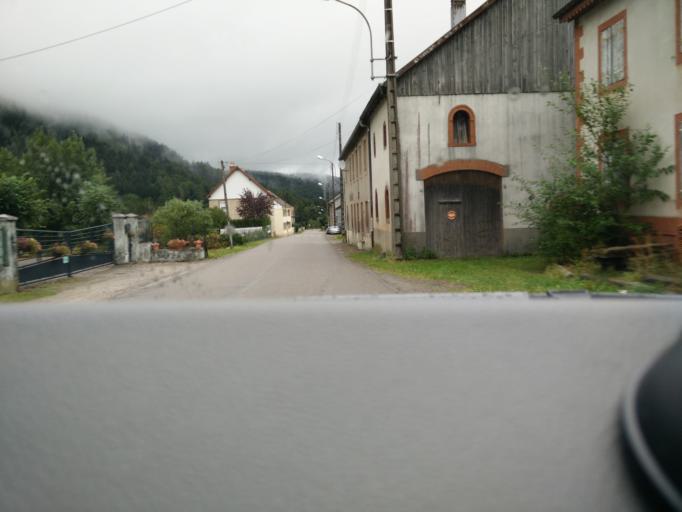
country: FR
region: Lorraine
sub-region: Departement des Vosges
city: Plainfaing
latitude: 48.1548
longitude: 7.0085
